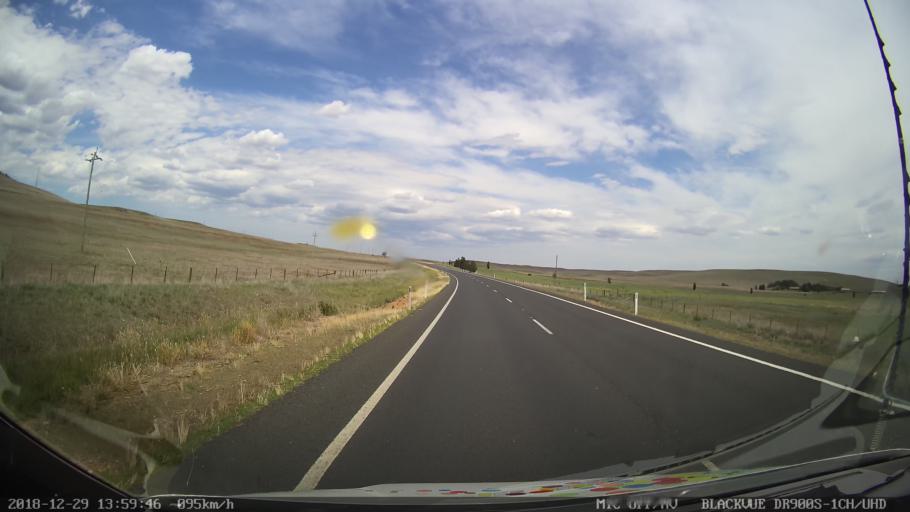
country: AU
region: New South Wales
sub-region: Cooma-Monaro
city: Cooma
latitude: -36.2572
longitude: 149.1509
